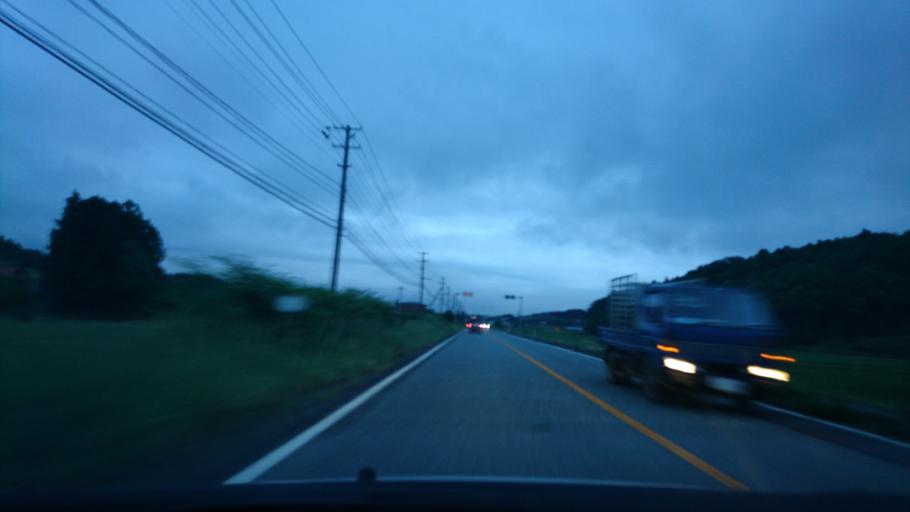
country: JP
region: Iwate
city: Ichinoseki
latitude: 38.8238
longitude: 141.0795
